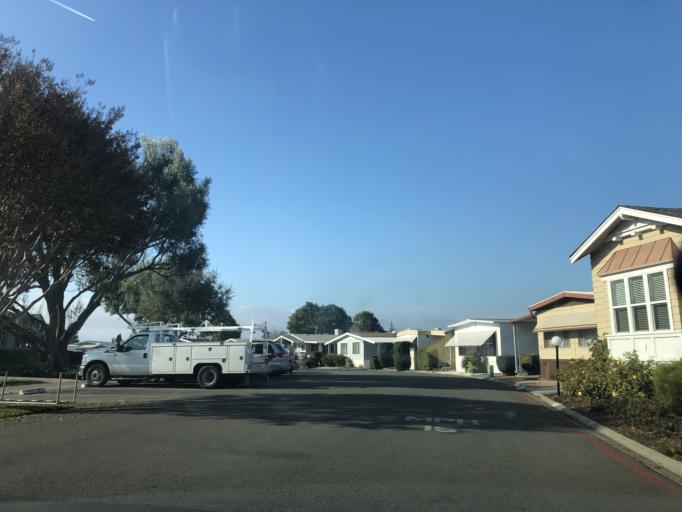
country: US
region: California
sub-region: Santa Clara County
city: Sunnyvale
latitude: 37.4018
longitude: -121.9930
